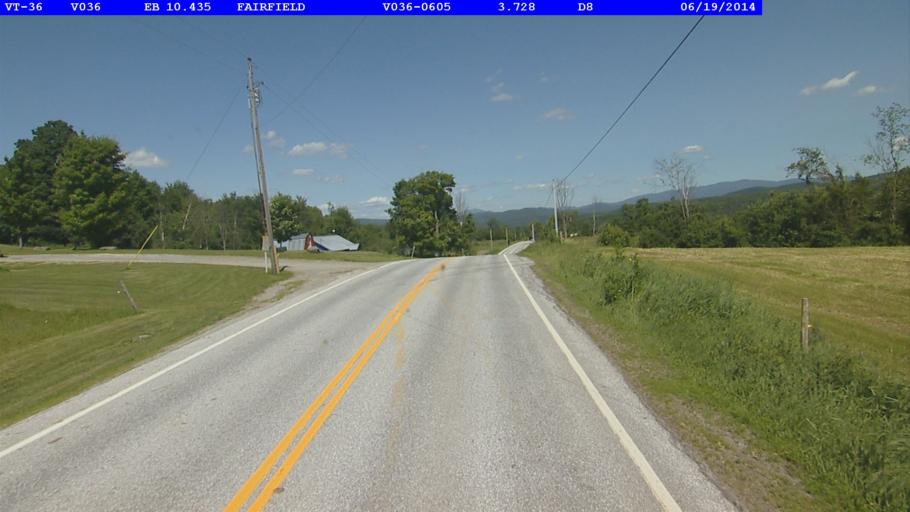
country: US
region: Vermont
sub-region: Franklin County
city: Saint Albans
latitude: 44.7984
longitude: -72.9595
